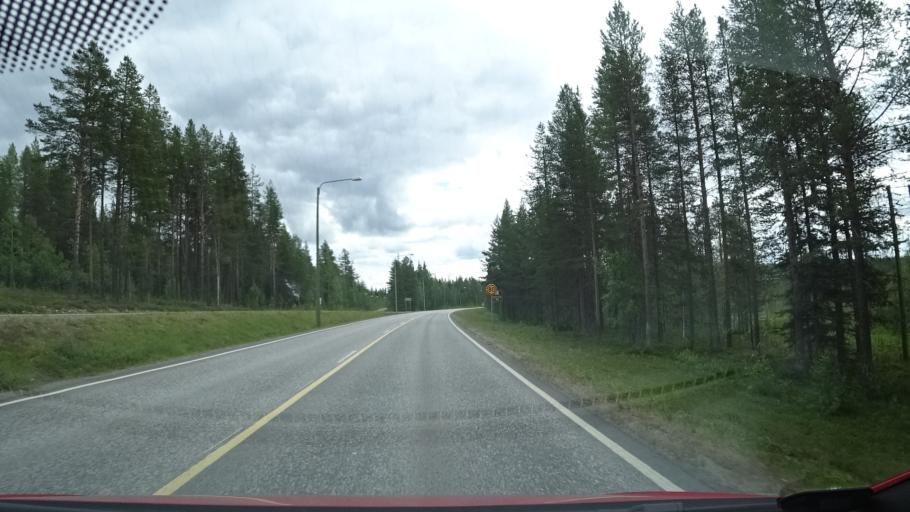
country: FI
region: Lapland
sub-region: Tunturi-Lappi
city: Kittilae
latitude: 67.7718
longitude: 24.8380
